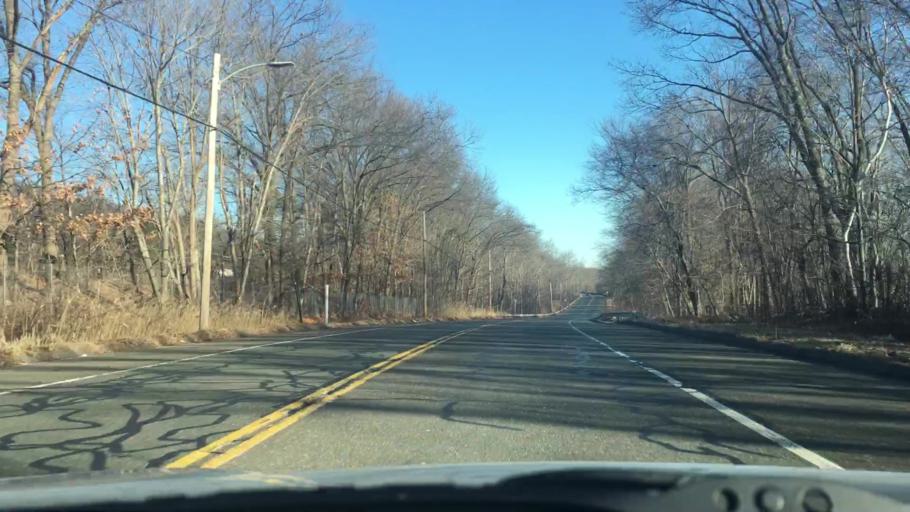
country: US
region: Massachusetts
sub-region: Hampden County
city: Ludlow
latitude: 42.1623
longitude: -72.5224
